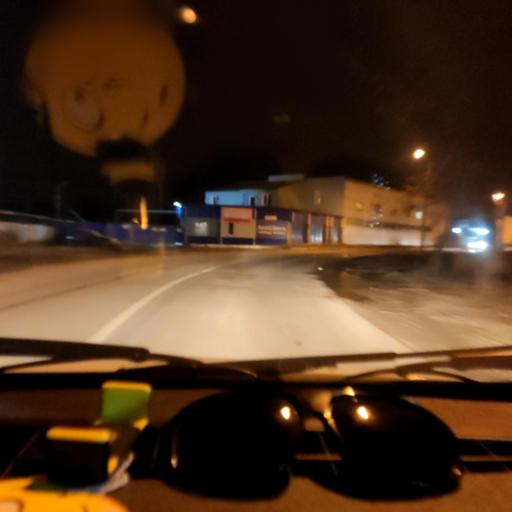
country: RU
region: Bashkortostan
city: Ufa
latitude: 54.8056
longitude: 56.0717
